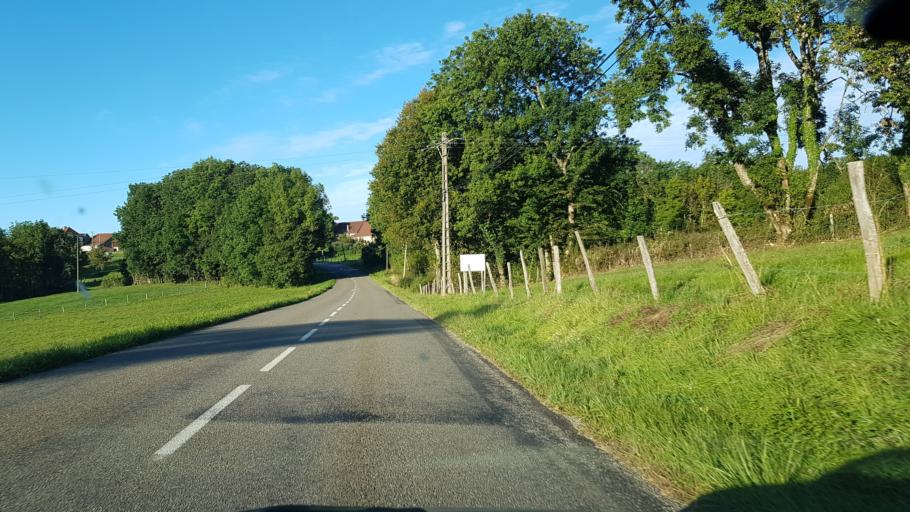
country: FR
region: Franche-Comte
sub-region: Departement du Jura
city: Lons-le-Saunier
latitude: 46.6290
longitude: 5.5331
